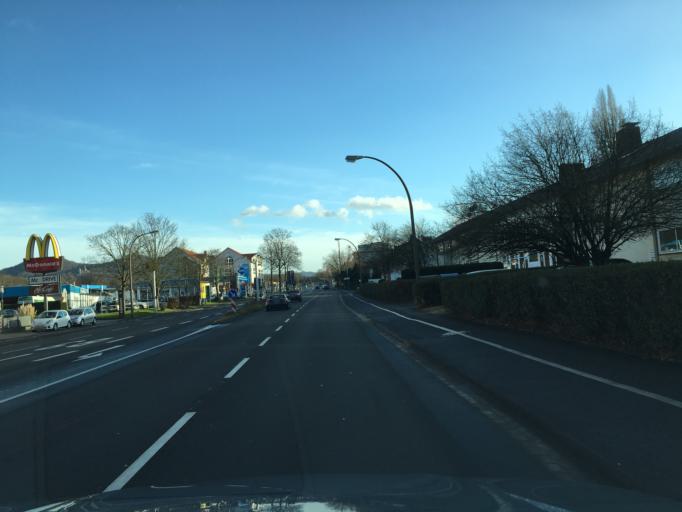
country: DE
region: North Rhine-Westphalia
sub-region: Regierungsbezirk Koln
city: Konigswinter
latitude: 50.6784
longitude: 7.1666
